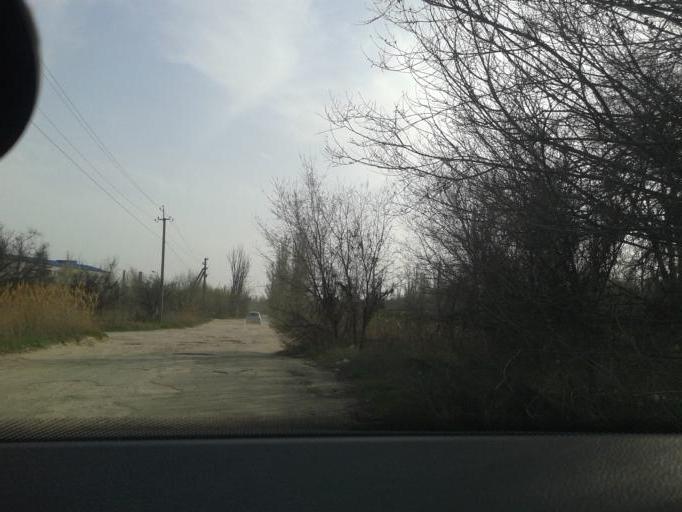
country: RU
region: Volgograd
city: Volgograd
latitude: 48.6347
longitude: 44.4386
